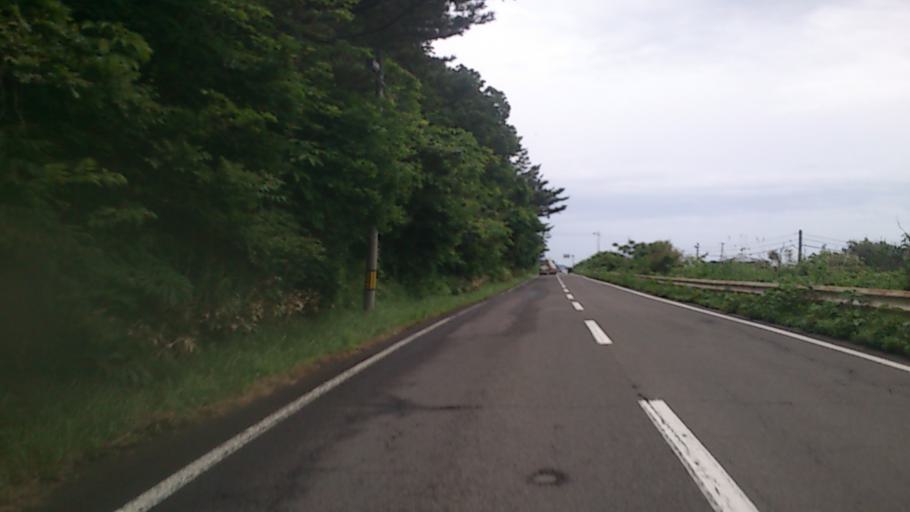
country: JP
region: Akita
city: Noshiromachi
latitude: 40.5156
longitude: 139.9511
